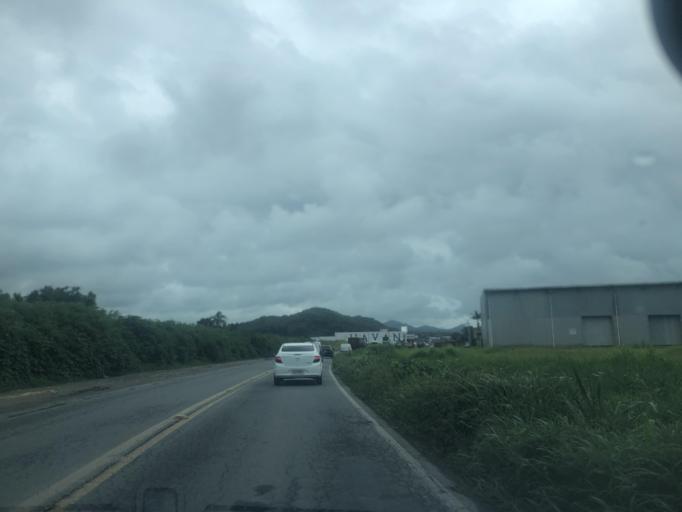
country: BR
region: Santa Catarina
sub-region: Sao Francisco Do Sul
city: Sao Francisco do Sul
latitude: -26.2489
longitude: -48.6157
